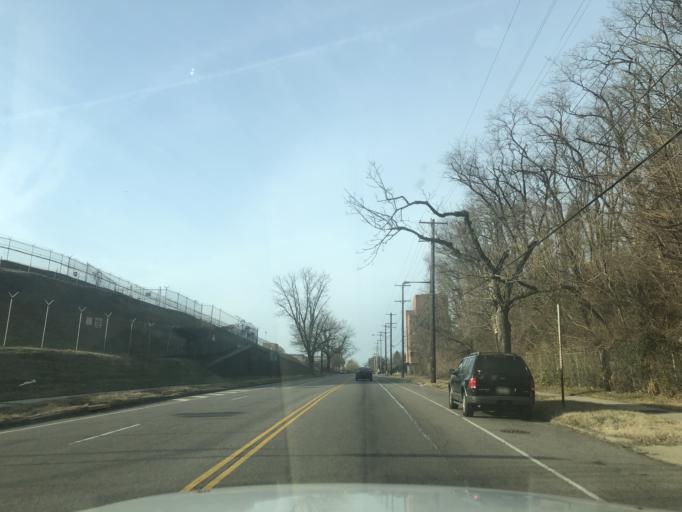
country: US
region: Pennsylvania
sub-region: Montgomery County
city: Bala-Cynwyd
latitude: 40.0151
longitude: -75.1789
